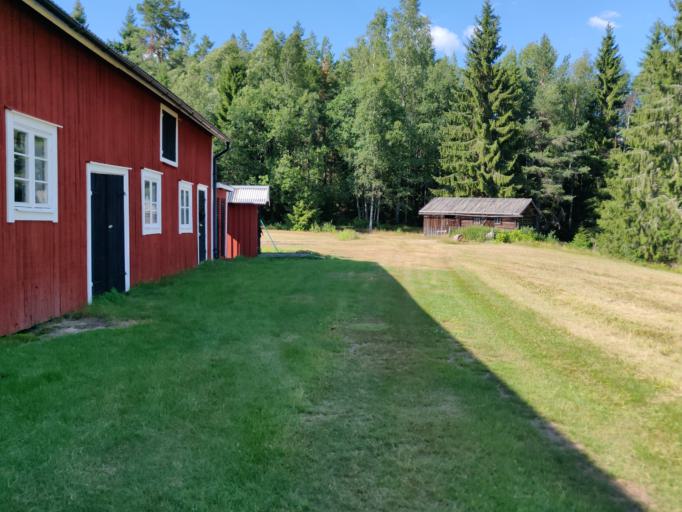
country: SE
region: Vaermland
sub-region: Hagfors Kommun
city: Ekshaerad
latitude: 60.1010
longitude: 13.3724
